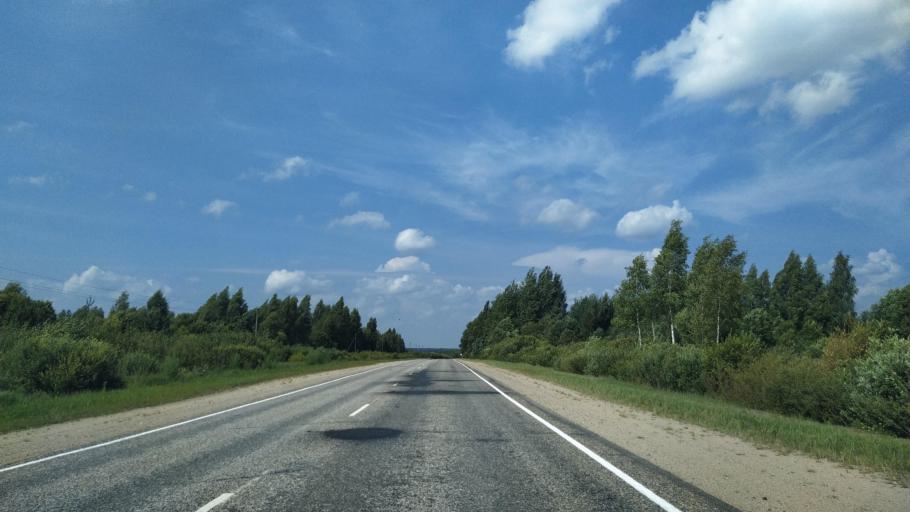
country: RU
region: Pskov
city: Pushkinskiye Gory
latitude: 57.0133
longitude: 28.8953
